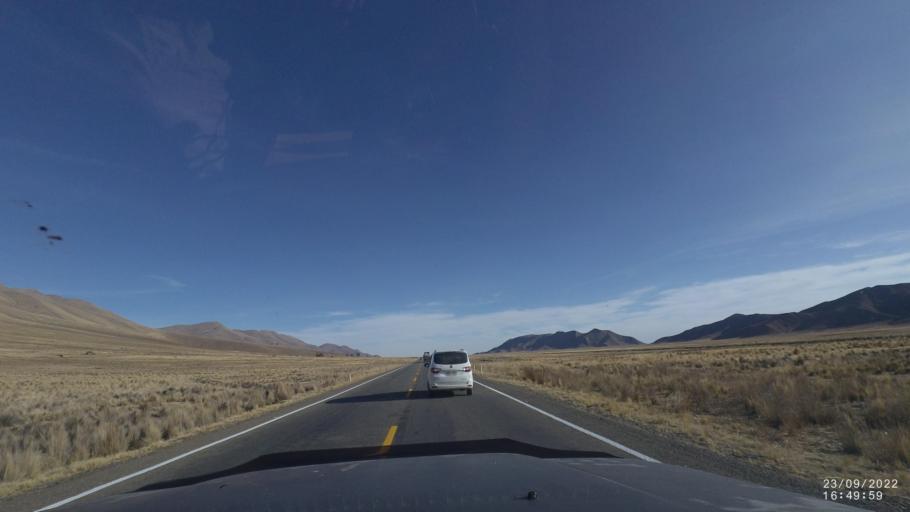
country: BO
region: Oruro
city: Poopo
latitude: -18.3968
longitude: -66.9778
